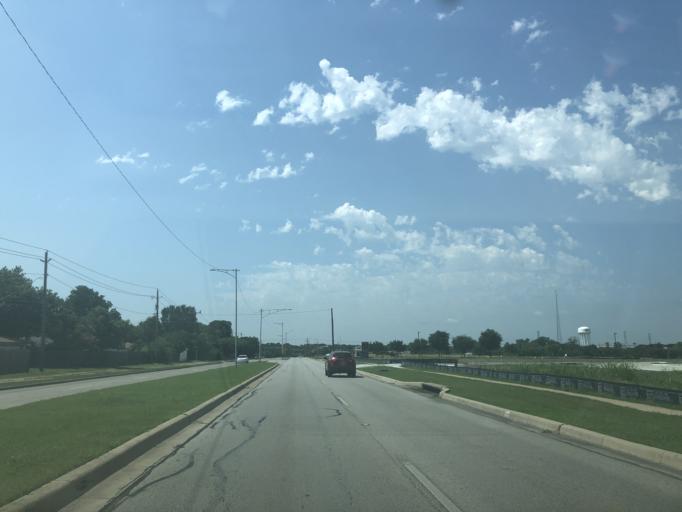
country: US
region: Texas
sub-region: Dallas County
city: Grand Prairie
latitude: 32.7319
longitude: -97.0147
